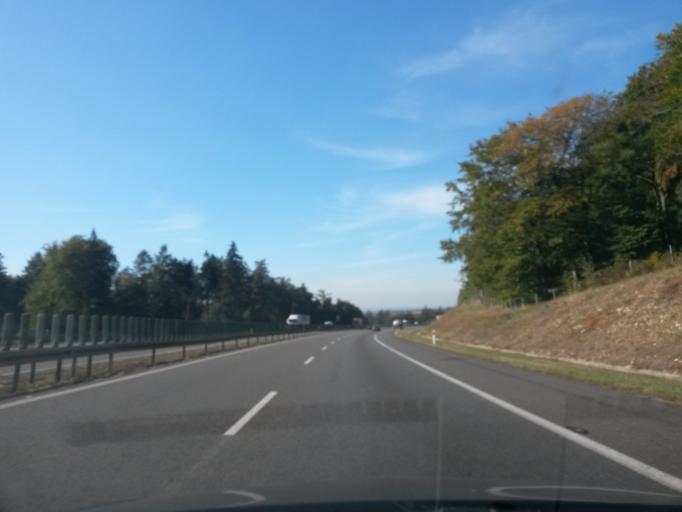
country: PL
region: Opole Voivodeship
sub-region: Powiat krapkowicki
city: Zdzieszowice
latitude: 50.4707
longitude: 18.1431
